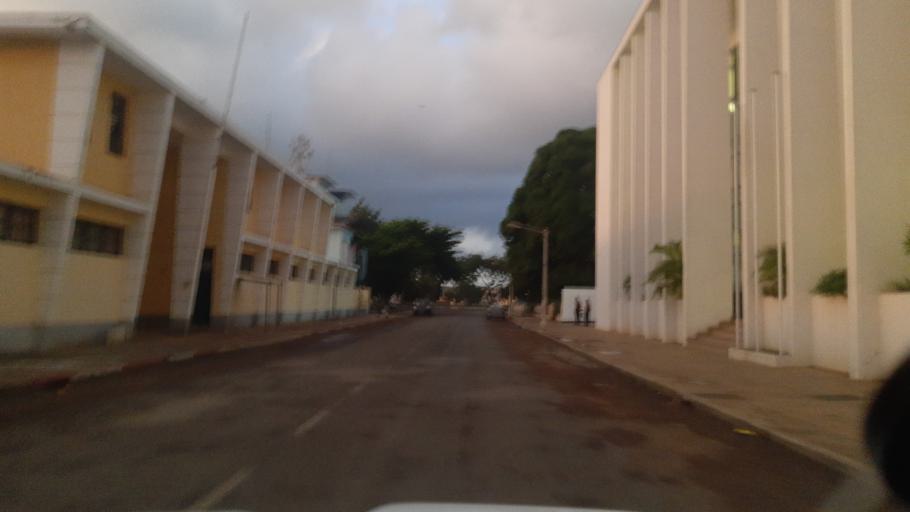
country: ST
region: Sao Tome Island
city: Sao Tome
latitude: 0.3438
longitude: 6.7363
